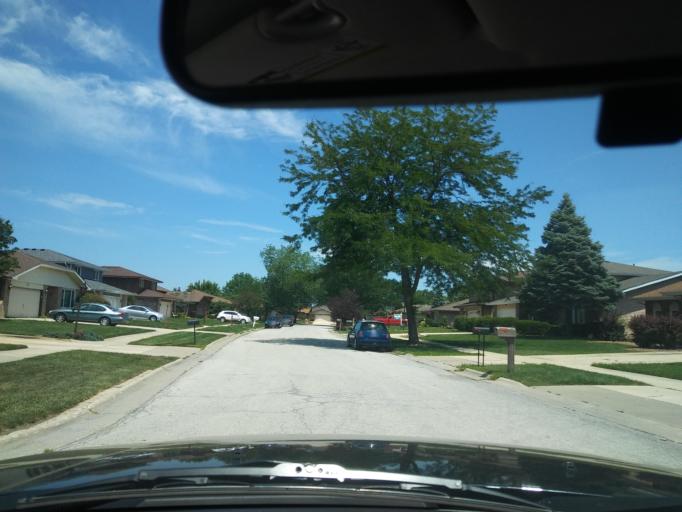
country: US
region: Illinois
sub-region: Cook County
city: Oak Forest
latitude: 41.6052
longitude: -87.7668
